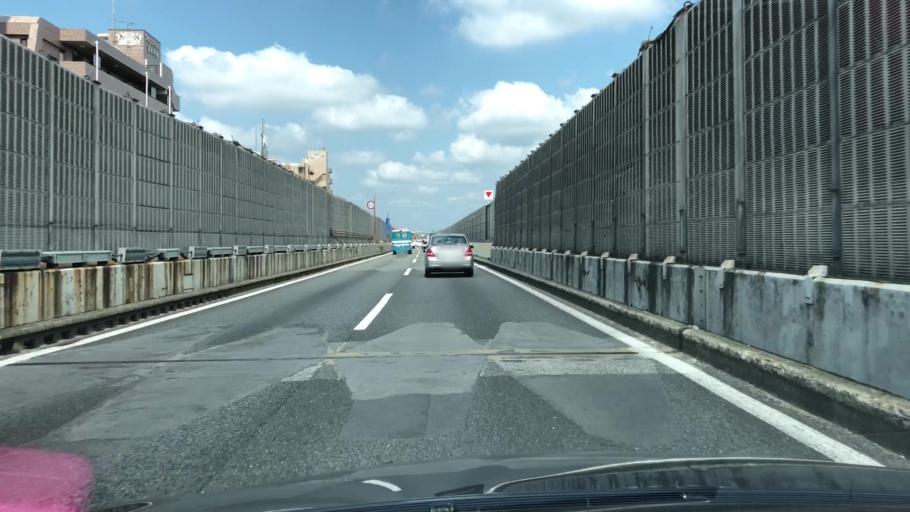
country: JP
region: Tokyo
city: Mitaka-shi
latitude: 35.6787
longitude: 139.6111
